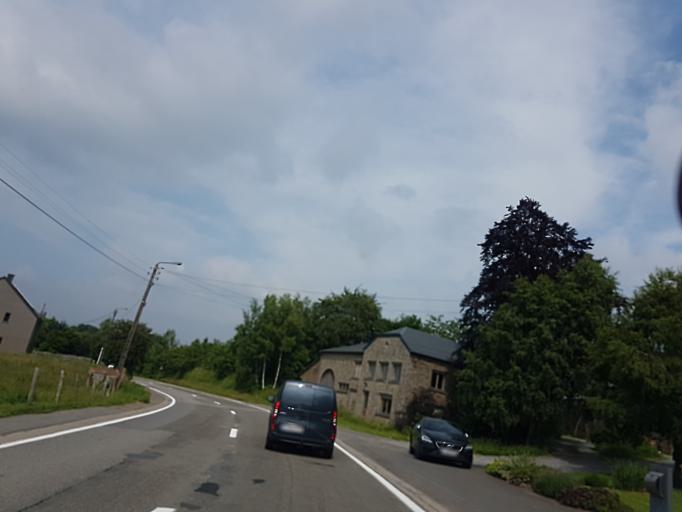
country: BE
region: Wallonia
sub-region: Province du Luxembourg
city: Manhay
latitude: 50.3019
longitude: 5.6991
